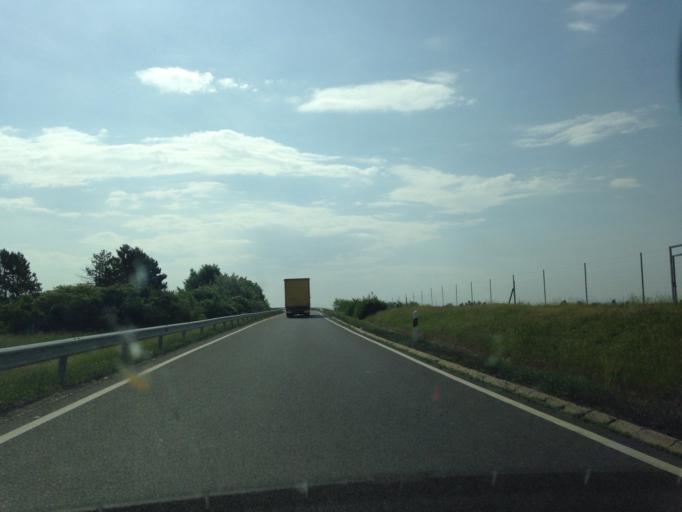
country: HU
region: Komarom-Esztergom
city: Tata
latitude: 47.6244
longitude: 18.3127
